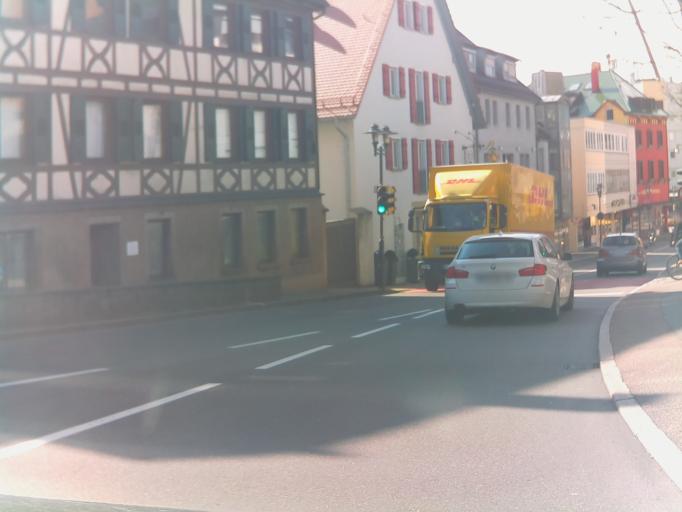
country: DE
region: Baden-Wuerttemberg
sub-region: Karlsruhe Region
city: Horb am Neckar
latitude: 48.4448
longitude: 8.6931
